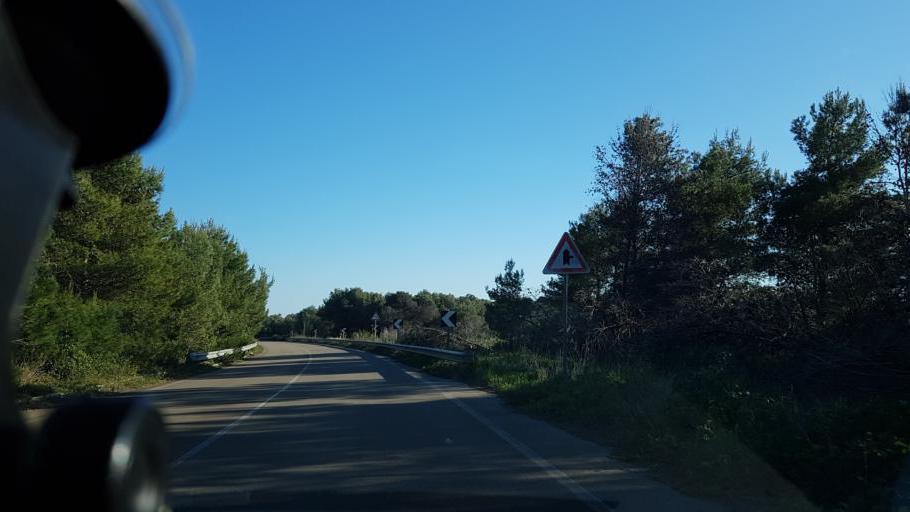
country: IT
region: Apulia
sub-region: Provincia di Lecce
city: Merine
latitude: 40.3998
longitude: 18.2499
